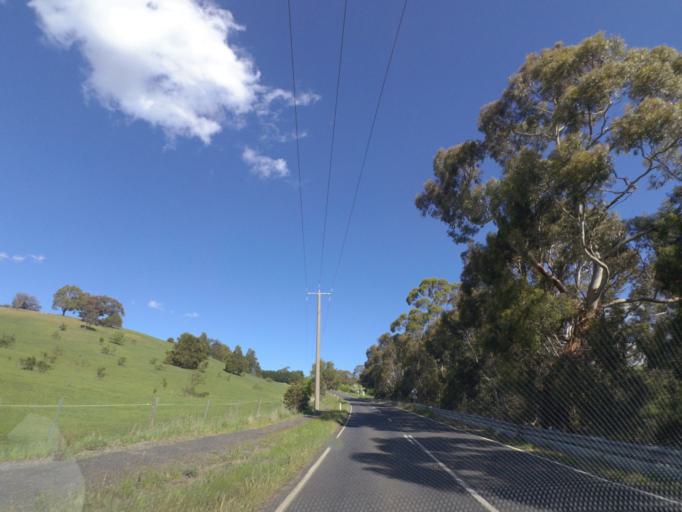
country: AU
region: Victoria
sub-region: Moorabool
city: Bacchus Marsh
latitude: -37.5655
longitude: 144.3083
